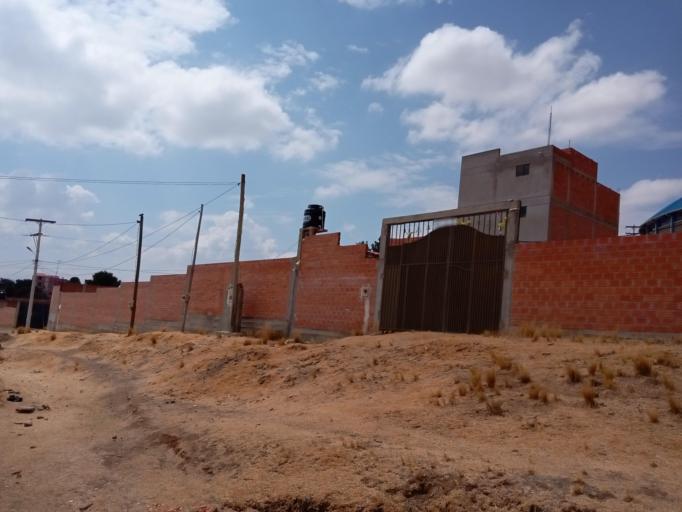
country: BO
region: La Paz
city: Batallas
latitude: -16.4004
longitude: -68.4804
